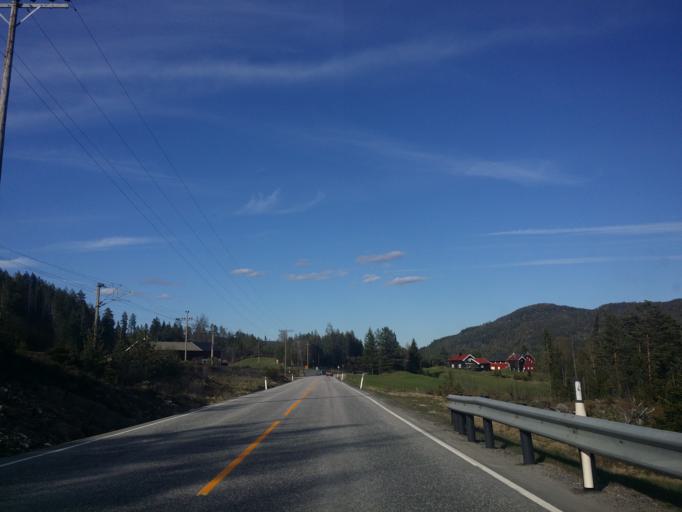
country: NO
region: Telemark
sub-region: Notodden
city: Notodden
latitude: 59.6094
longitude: 9.4488
